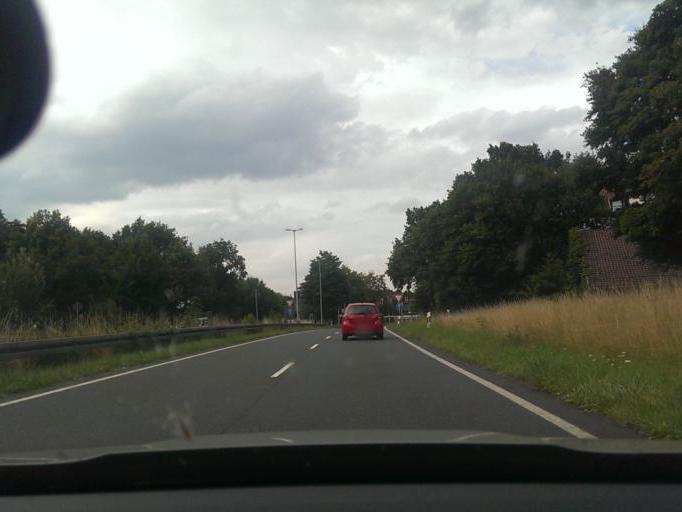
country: DE
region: Lower Saxony
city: Hannover
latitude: 52.3908
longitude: 9.6867
